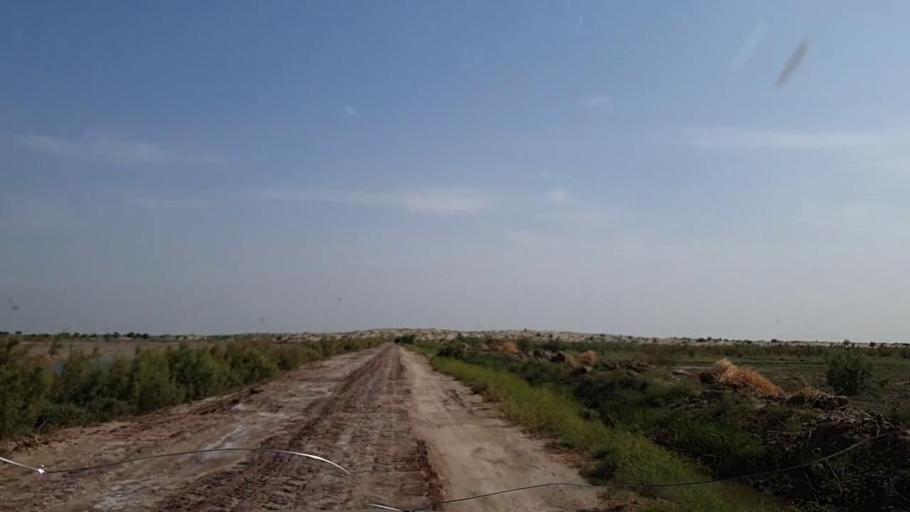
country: PK
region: Sindh
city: Khanpur
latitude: 27.6786
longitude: 69.3683
